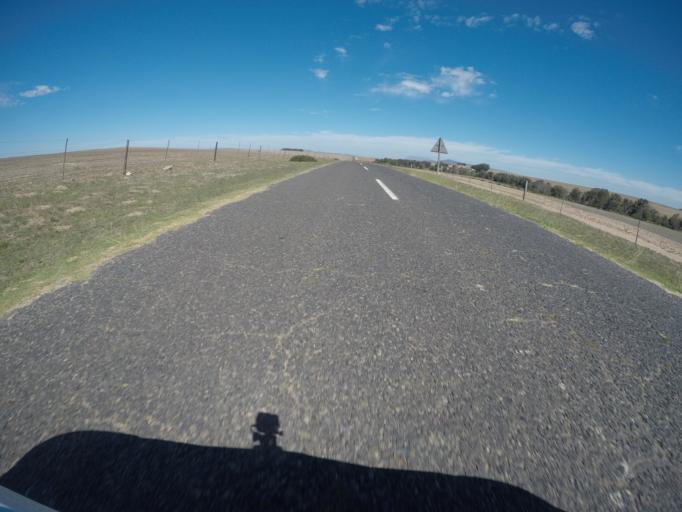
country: ZA
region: Western Cape
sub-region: City of Cape Town
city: Atlantis
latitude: -33.6212
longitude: 18.6322
